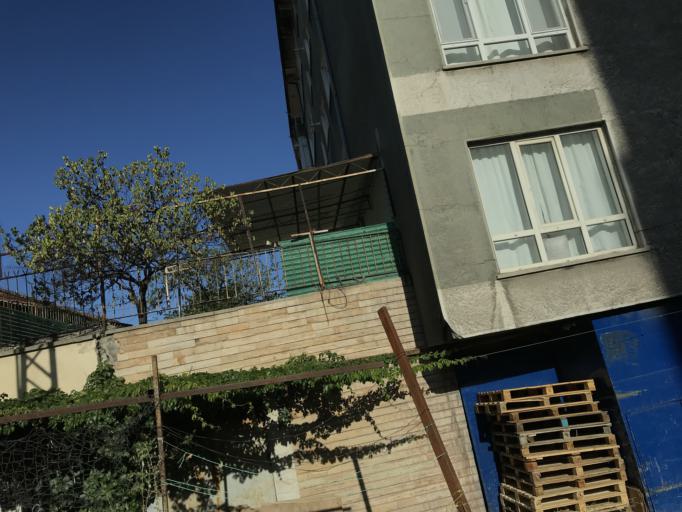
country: TR
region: Ankara
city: Cankaya
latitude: 39.9374
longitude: 32.8695
